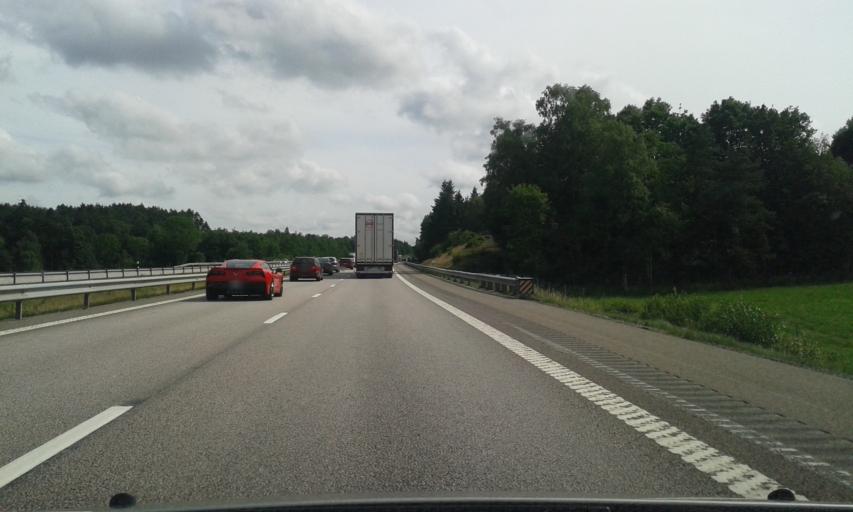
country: SE
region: Halland
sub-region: Kungsbacka Kommun
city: Frillesas
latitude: 57.3616
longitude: 12.2074
